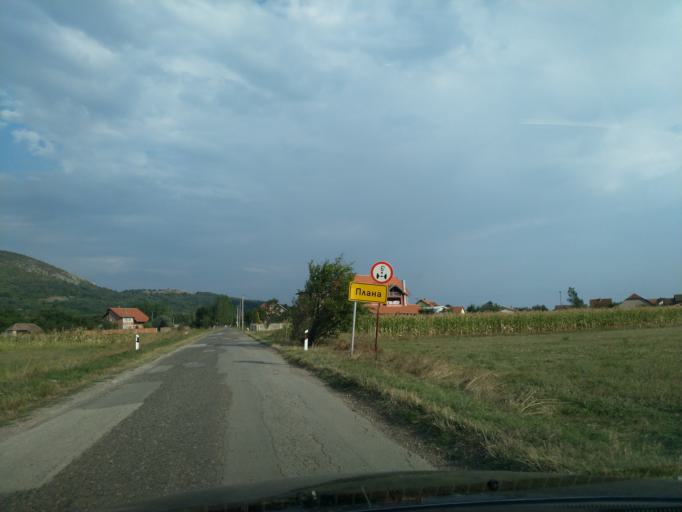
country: RS
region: Central Serbia
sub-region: Pomoravski Okrug
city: Paracin
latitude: 43.8227
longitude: 21.5362
